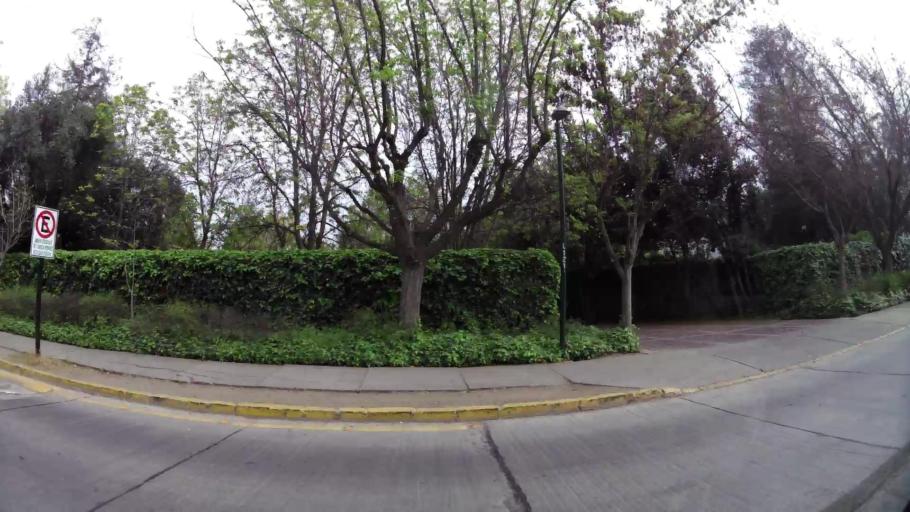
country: CL
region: Santiago Metropolitan
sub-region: Provincia de Santiago
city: Villa Presidente Frei, Nunoa, Santiago, Chile
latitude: -33.3791
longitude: -70.5327
